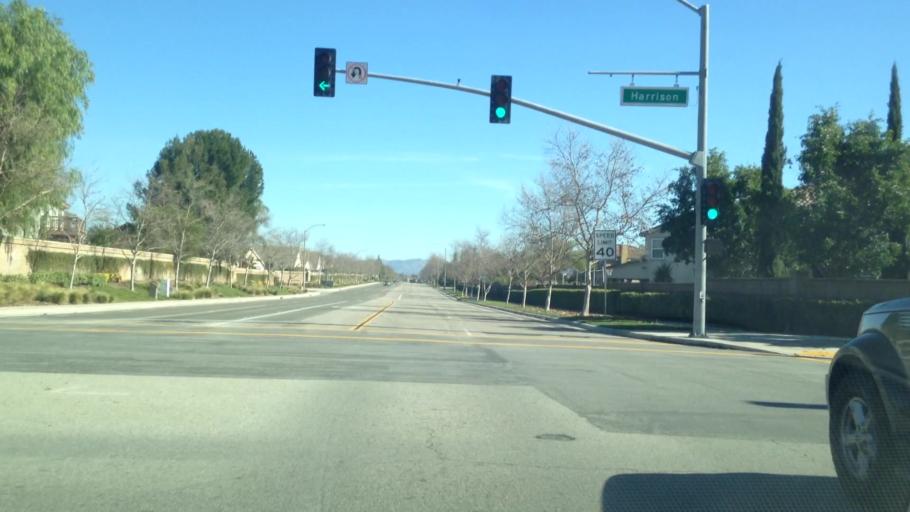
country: US
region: California
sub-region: Riverside County
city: Norco
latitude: 33.9681
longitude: -117.5846
